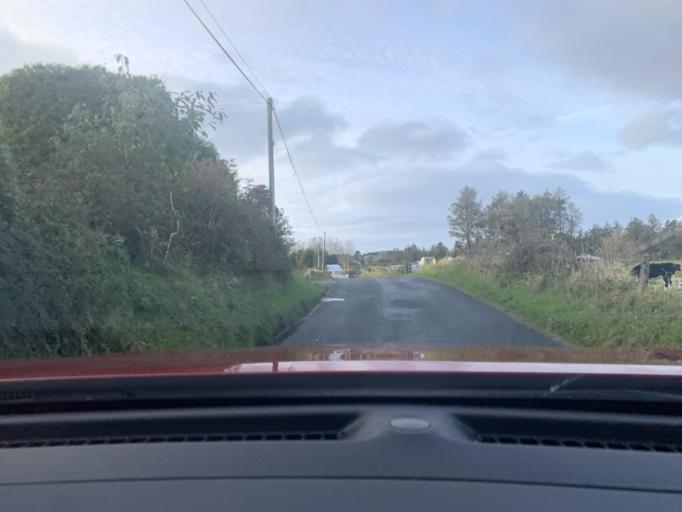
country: IE
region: Connaught
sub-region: Roscommon
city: Ballaghaderreen
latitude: 53.9152
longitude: -8.5900
